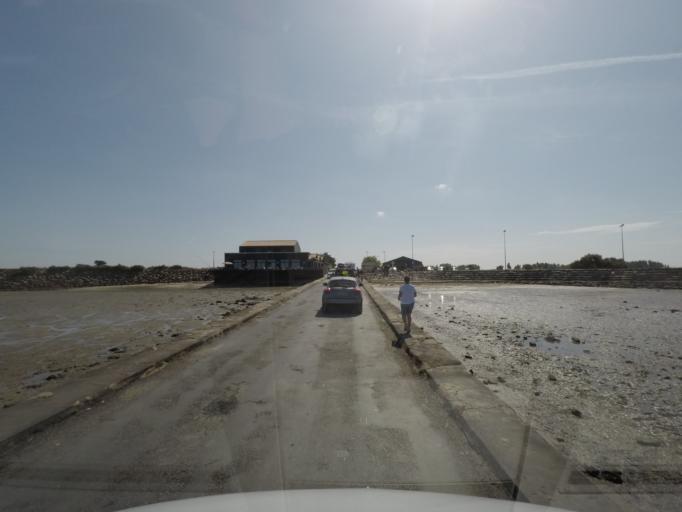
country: FR
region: Pays de la Loire
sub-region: Departement de la Vendee
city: La Barre-de-Monts
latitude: 46.9215
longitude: -2.1045
